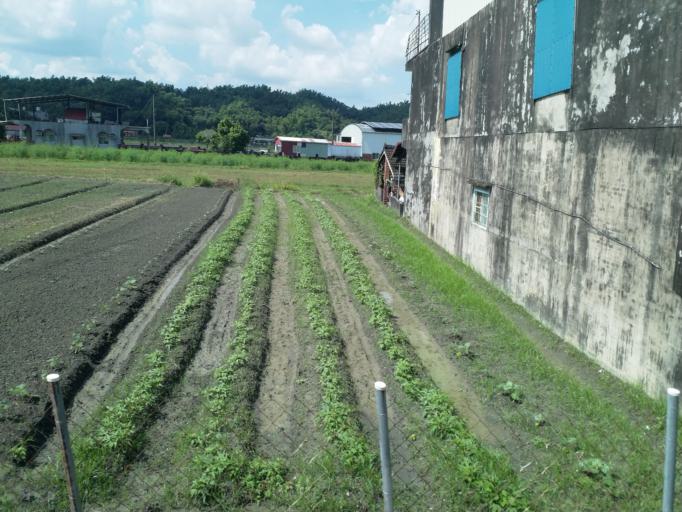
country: TW
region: Taiwan
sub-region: Pingtung
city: Pingtung
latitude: 22.8835
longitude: 120.5768
